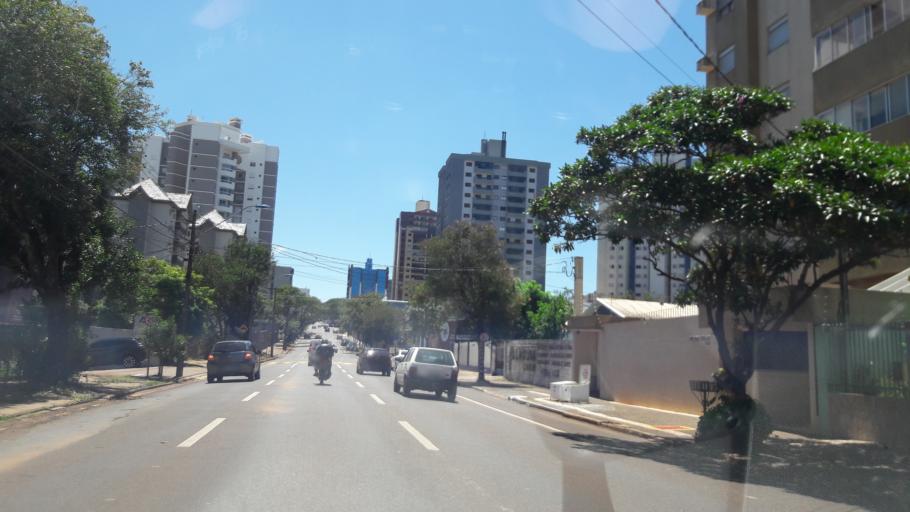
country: BR
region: Parana
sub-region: Cascavel
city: Cascavel
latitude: -24.9516
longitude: -53.4689
